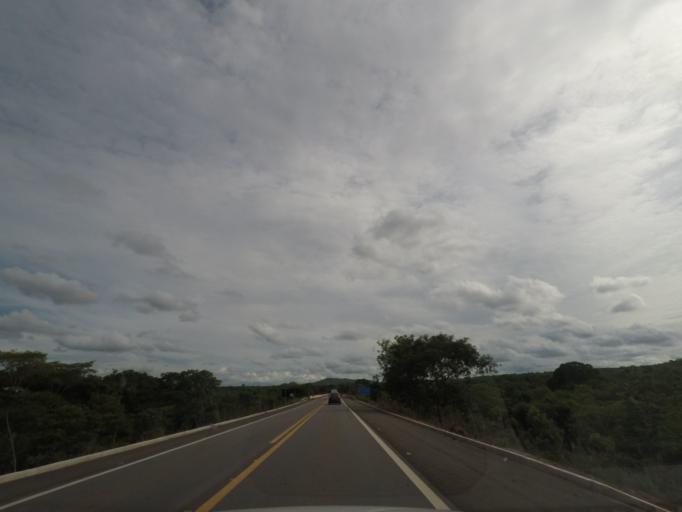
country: BR
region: Goias
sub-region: Uruacu
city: Uruacu
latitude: -14.7412
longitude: -49.0694
